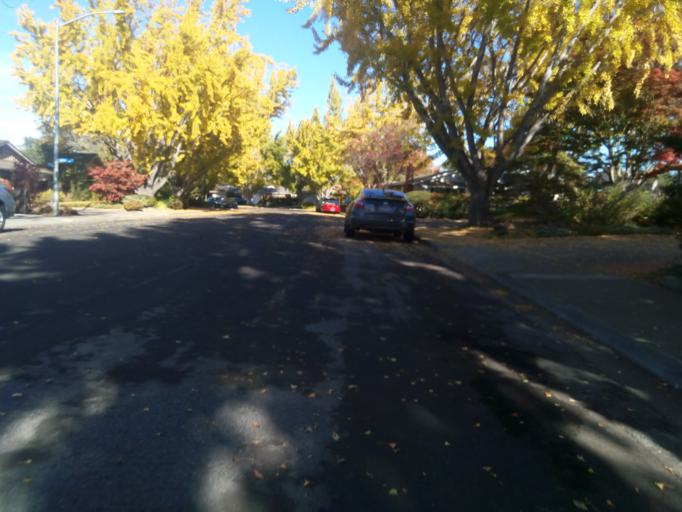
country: US
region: California
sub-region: Santa Clara County
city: Mountain View
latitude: 37.3743
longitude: -122.0819
